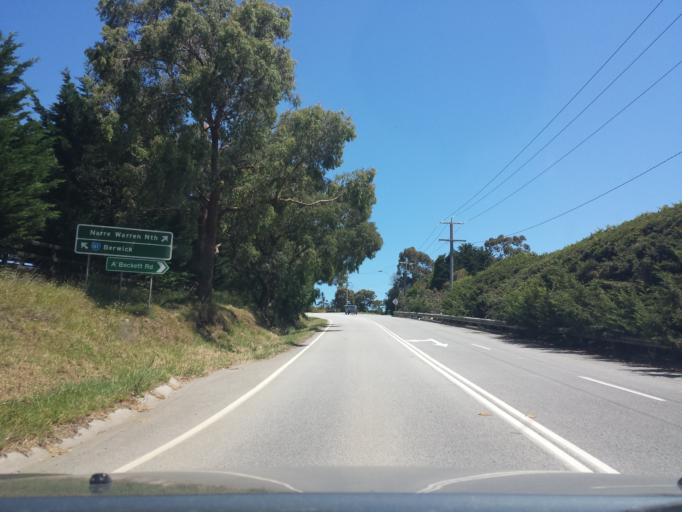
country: AU
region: Victoria
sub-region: Casey
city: Narre Warren North
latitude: -37.9800
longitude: 145.3549
